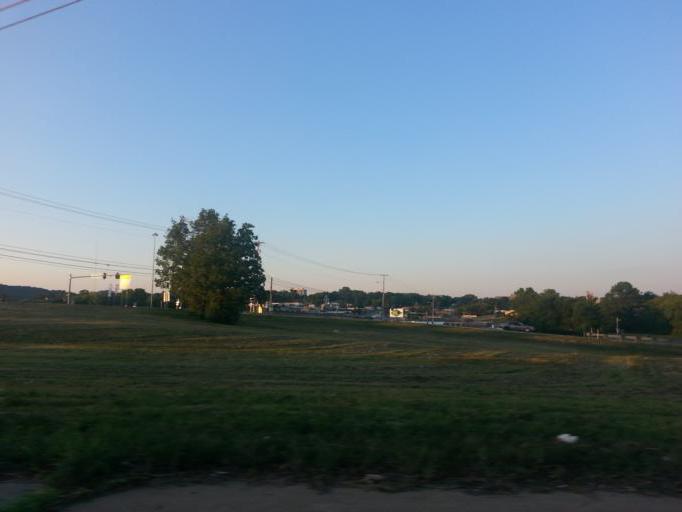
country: US
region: Tennessee
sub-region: Knox County
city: Knoxville
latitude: 35.9755
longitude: -83.9356
